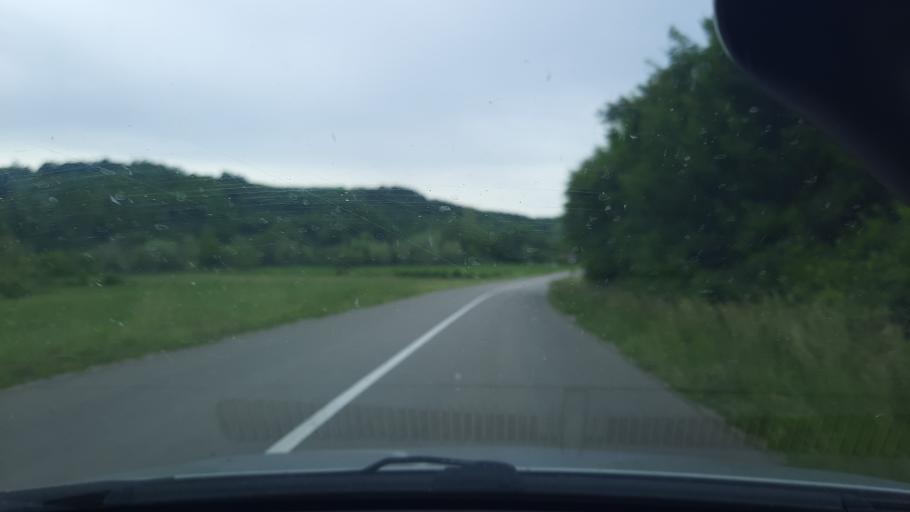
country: RS
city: Bukor
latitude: 44.5287
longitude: 19.5146
